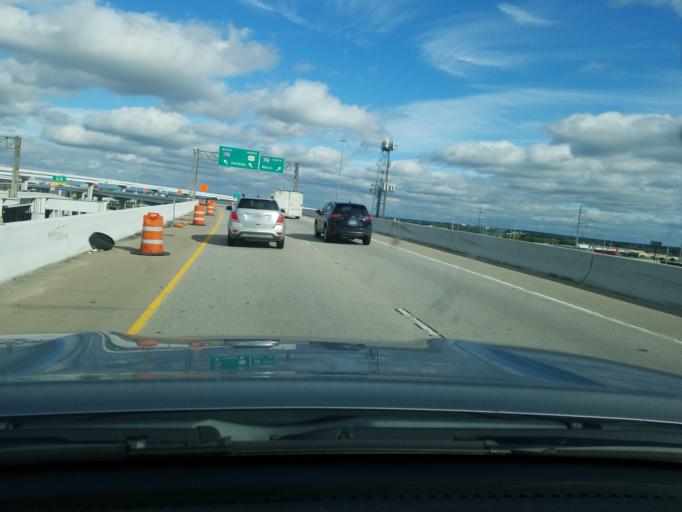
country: US
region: Texas
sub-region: Tarrant County
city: Fort Worth
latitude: 32.7446
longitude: -97.3250
